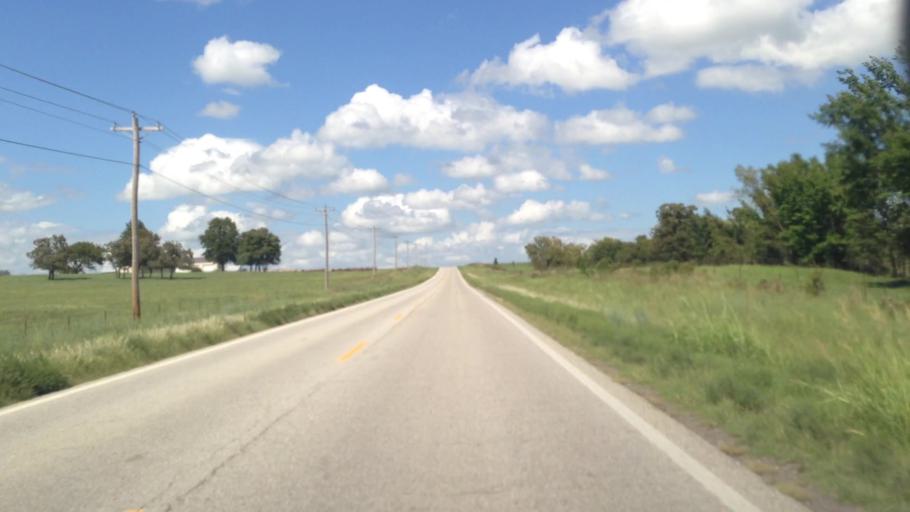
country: US
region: Oklahoma
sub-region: Craig County
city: Vinita
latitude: 36.7360
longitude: -95.1436
